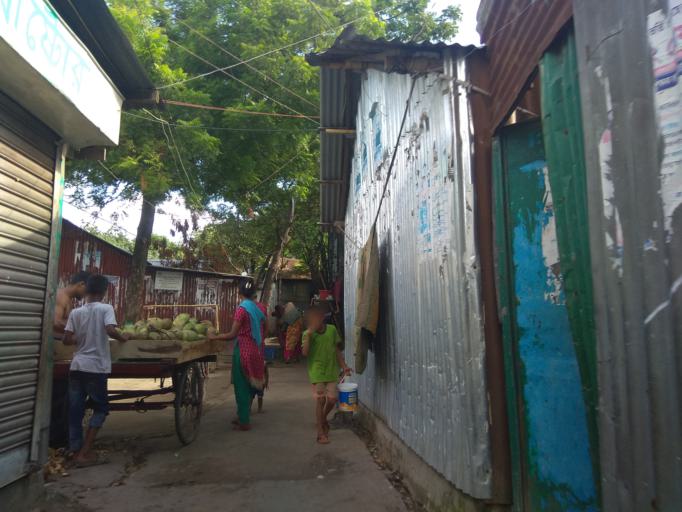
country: BD
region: Dhaka
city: Paltan
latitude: 23.8098
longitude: 90.3898
